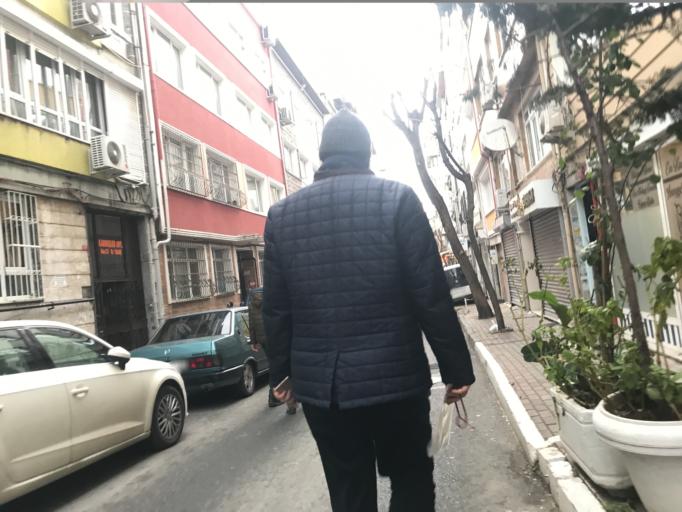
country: TR
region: Istanbul
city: Istanbul
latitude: 41.0174
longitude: 28.9484
